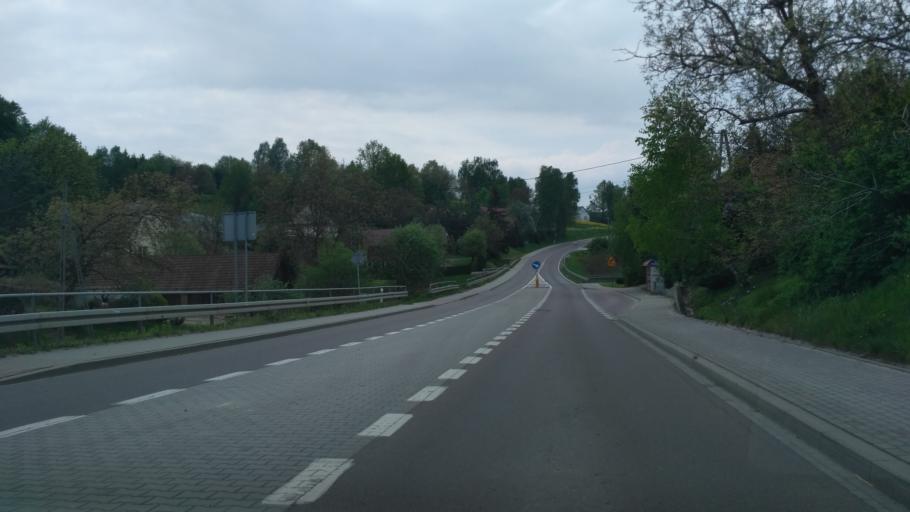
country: PL
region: Lesser Poland Voivodeship
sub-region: Powiat tarnowski
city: Tarnowiec
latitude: 49.9679
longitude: 20.9948
